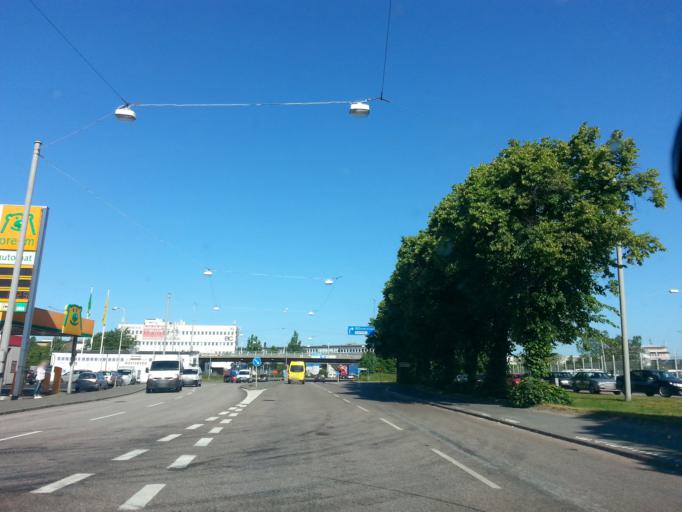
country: SE
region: Vaestra Goetaland
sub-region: Goteborg
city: Goeteborg
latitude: 57.7302
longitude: 12.0018
